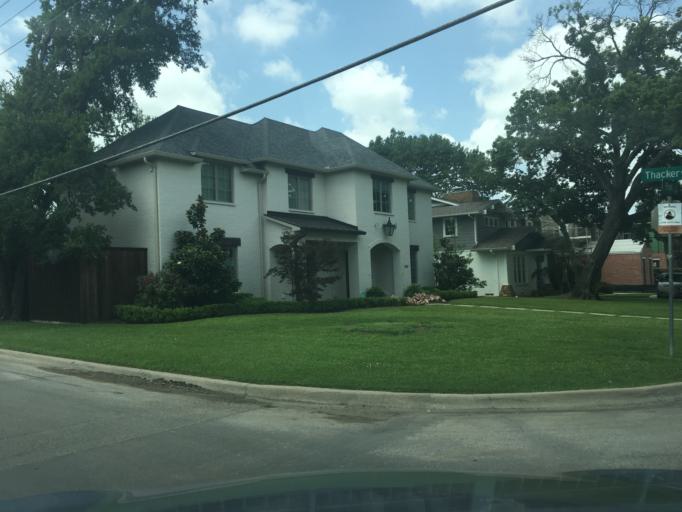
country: US
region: Texas
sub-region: Dallas County
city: University Park
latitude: 32.8735
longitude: -96.7916
